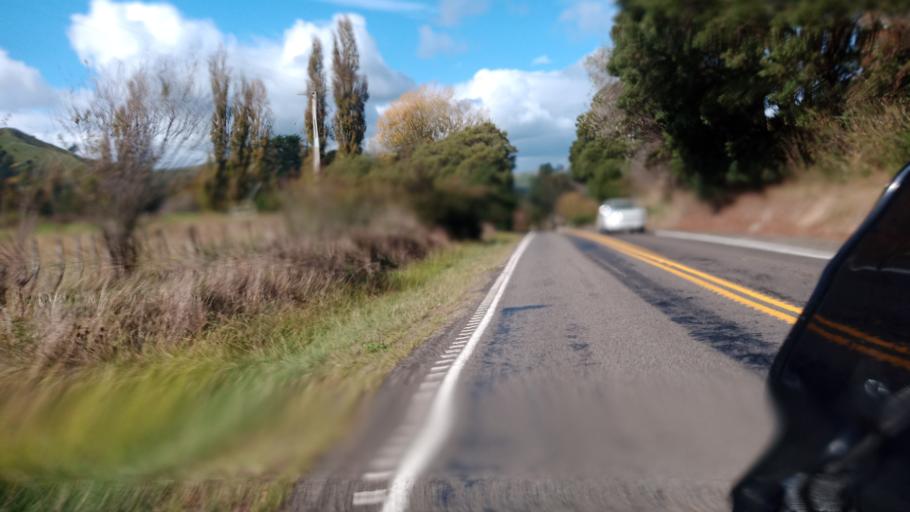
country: NZ
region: Gisborne
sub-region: Gisborne District
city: Gisborne
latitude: -38.4622
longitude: 177.6487
